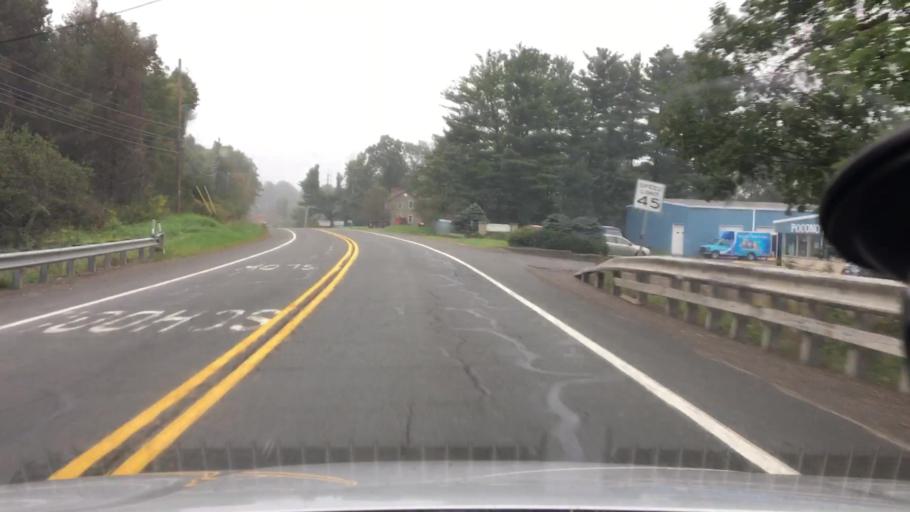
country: US
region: Pennsylvania
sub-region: Monroe County
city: Mountainhome
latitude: 41.1497
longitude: -75.2862
